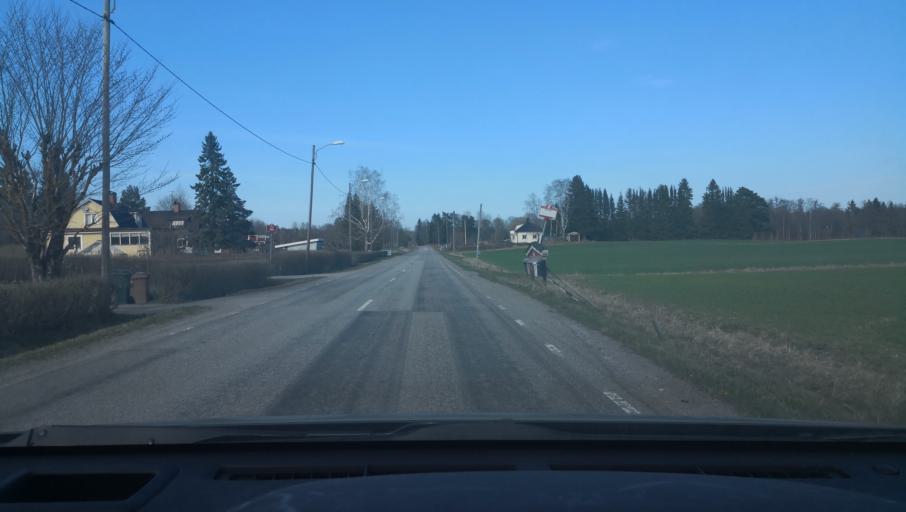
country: SE
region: Uppsala
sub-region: Heby Kommun
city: Heby
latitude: 59.9550
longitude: 16.8782
